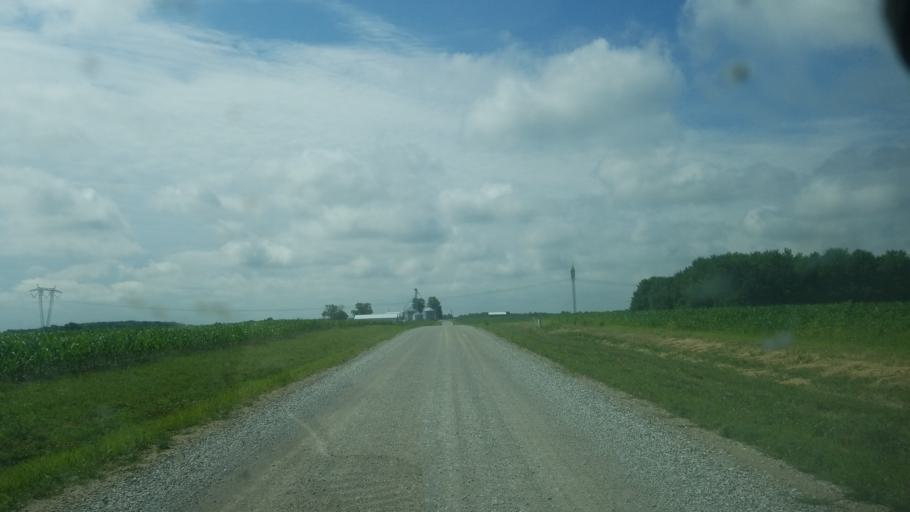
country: US
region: Ohio
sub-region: Licking County
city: Johnstown
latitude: 40.2146
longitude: -82.7394
